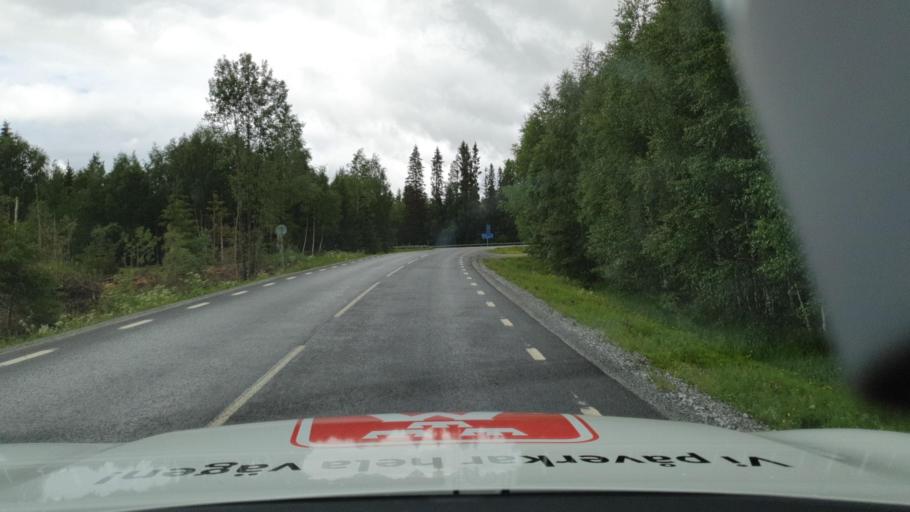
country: SE
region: Vaesterbotten
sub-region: Dorotea Kommun
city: Dorotea
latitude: 64.2480
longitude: 16.5304
